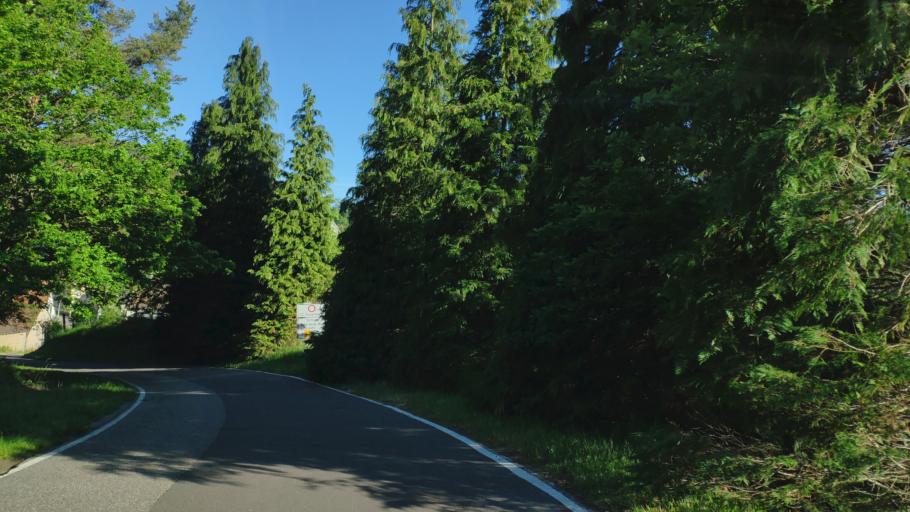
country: DE
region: Rheinland-Pfalz
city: Vorderweidenthal
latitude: 49.1119
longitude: 7.8636
